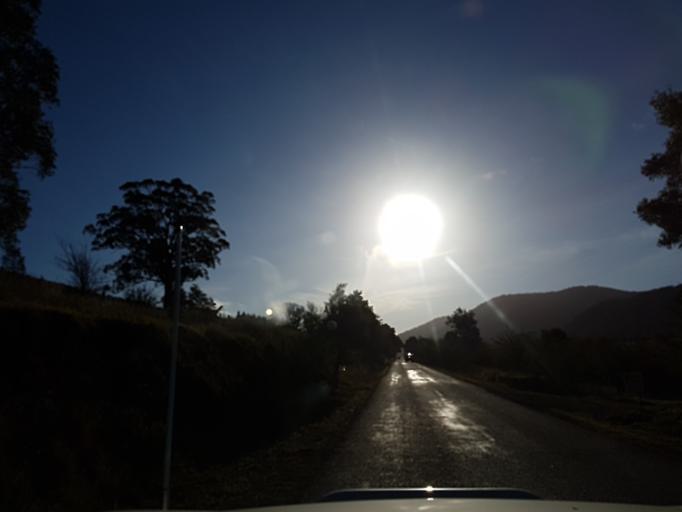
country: AU
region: Victoria
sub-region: East Gippsland
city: Bairnsdale
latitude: -37.4734
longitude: 147.2263
